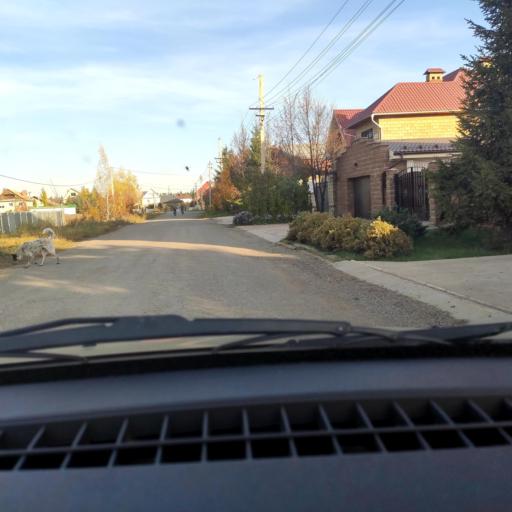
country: RU
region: Bashkortostan
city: Ufa
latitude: 54.6496
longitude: 55.9234
